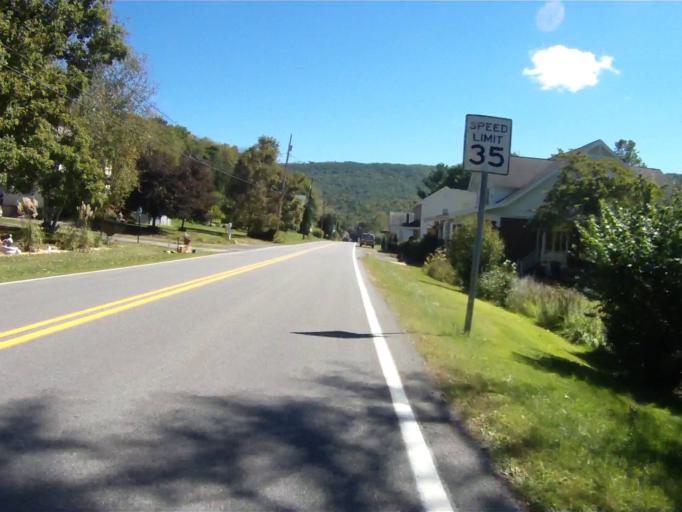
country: US
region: Pennsylvania
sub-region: Centre County
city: Houserville
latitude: 40.9086
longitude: -77.8800
